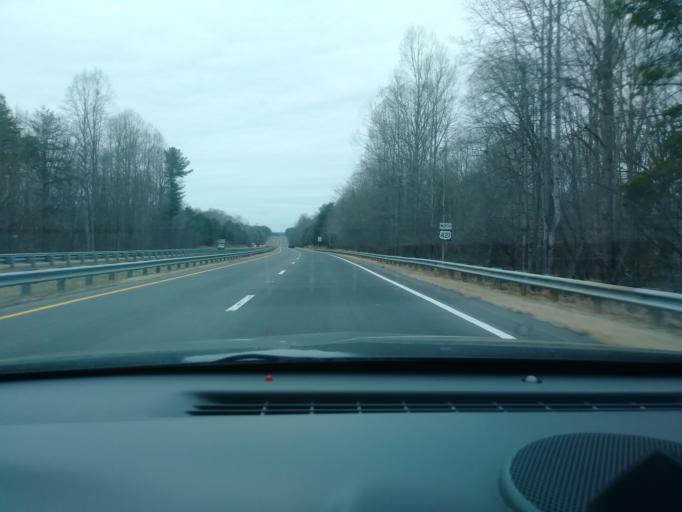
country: US
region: North Carolina
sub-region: Forsyth County
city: Lewisville
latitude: 36.1018
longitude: -80.4743
